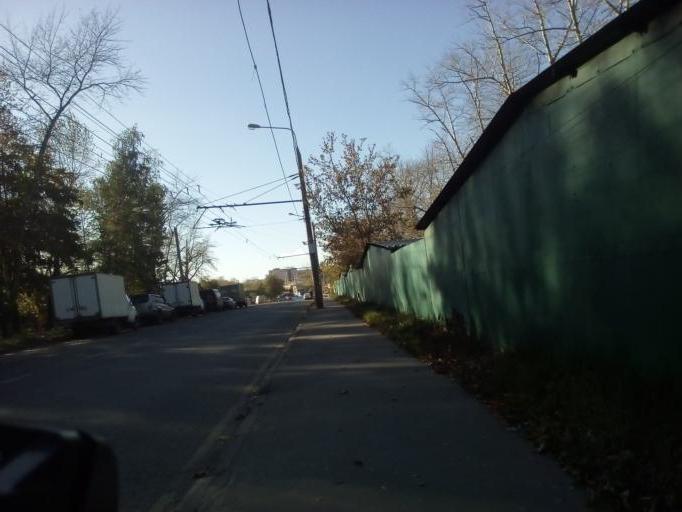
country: RU
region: Moscow
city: Likhobory
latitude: 55.8487
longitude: 37.5707
